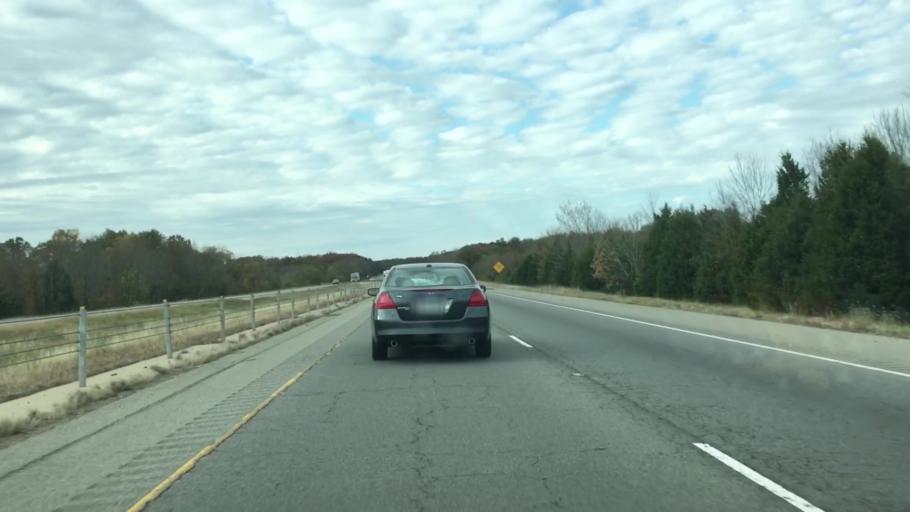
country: US
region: Arkansas
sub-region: Faulkner County
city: Conway
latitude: 35.1280
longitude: -92.5122
